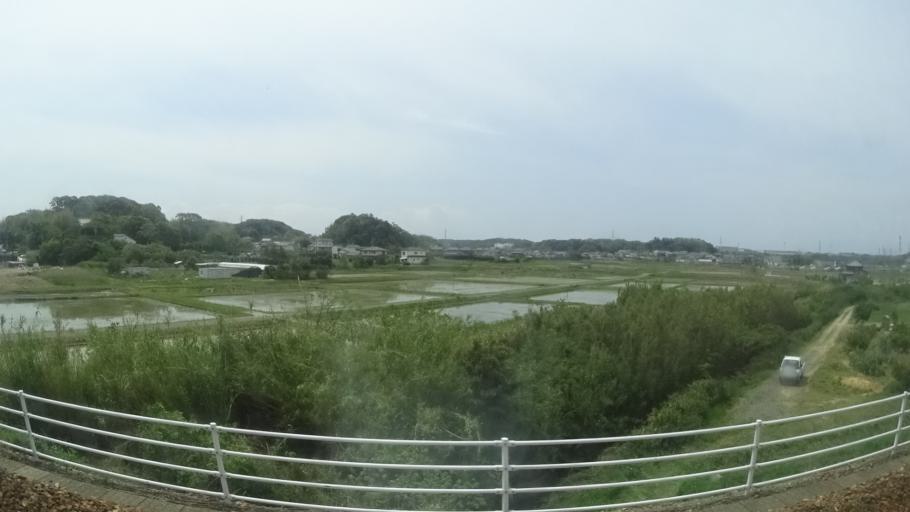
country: JP
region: Shizuoka
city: Kosai-shi
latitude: 34.7217
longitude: 137.5231
